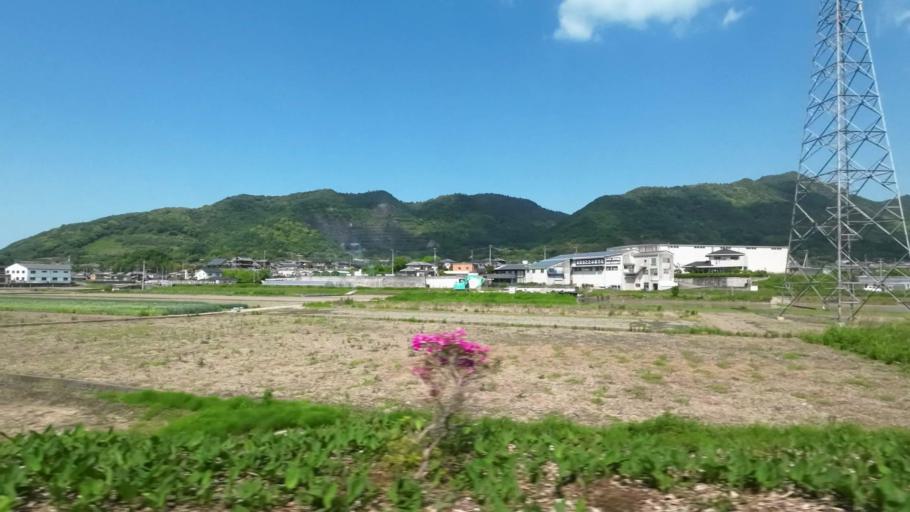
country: JP
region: Kagawa
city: Kan'onjicho
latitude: 34.1472
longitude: 133.6864
